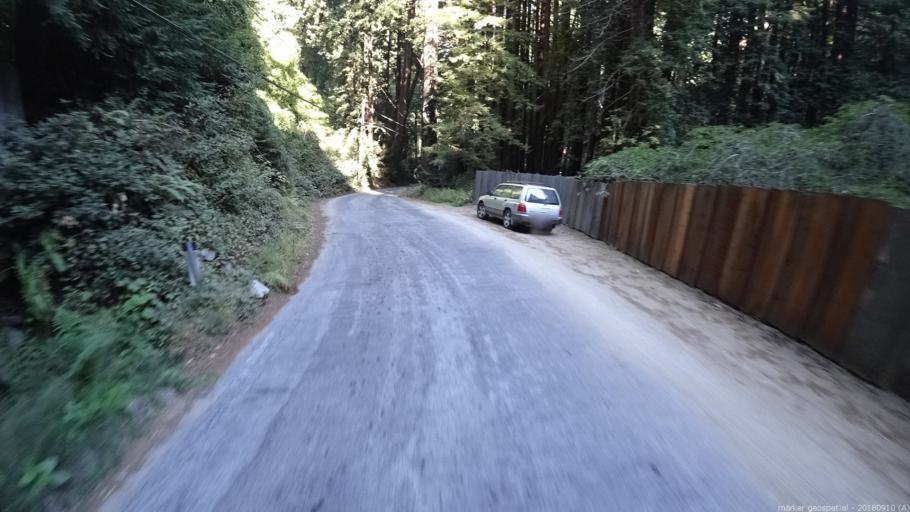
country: US
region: California
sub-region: Monterey County
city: Carmel Valley Village
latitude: 36.3933
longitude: -121.8775
